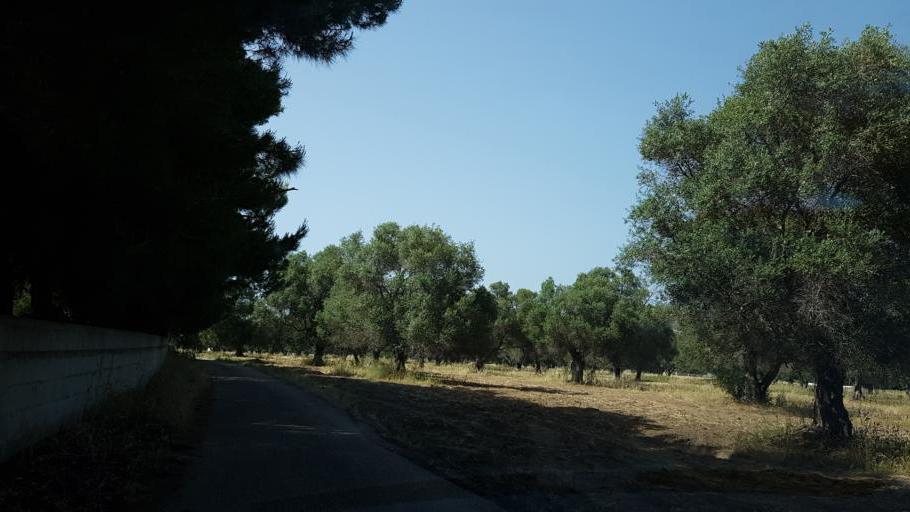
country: IT
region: Apulia
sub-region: Provincia di Brindisi
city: Brindisi
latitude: 40.6594
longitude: 17.9277
